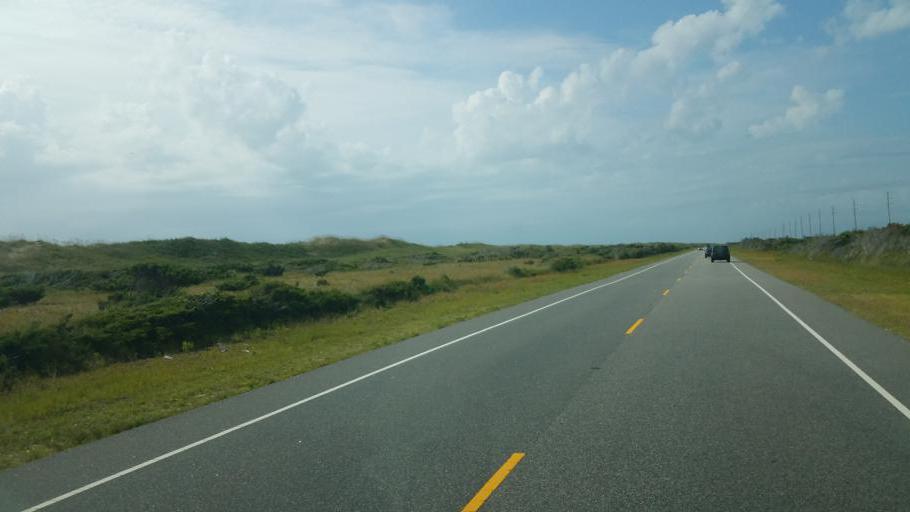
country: US
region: North Carolina
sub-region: Dare County
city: Buxton
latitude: 35.3061
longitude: -75.5122
